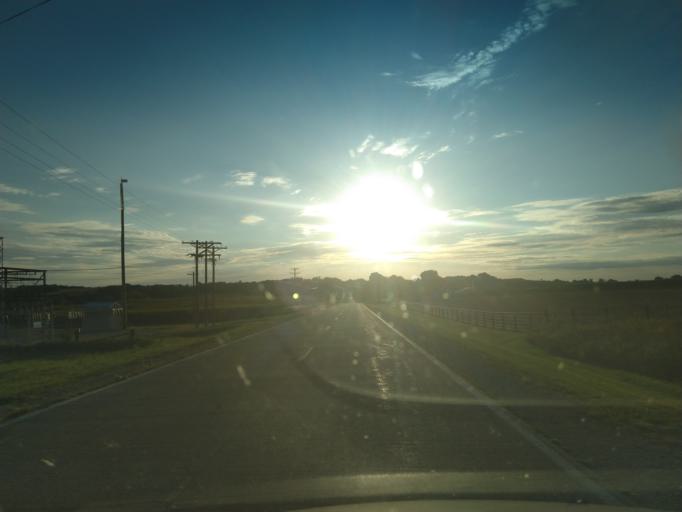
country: US
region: Iowa
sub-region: Jackson County
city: Maquoketa
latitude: 42.1643
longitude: -90.7184
